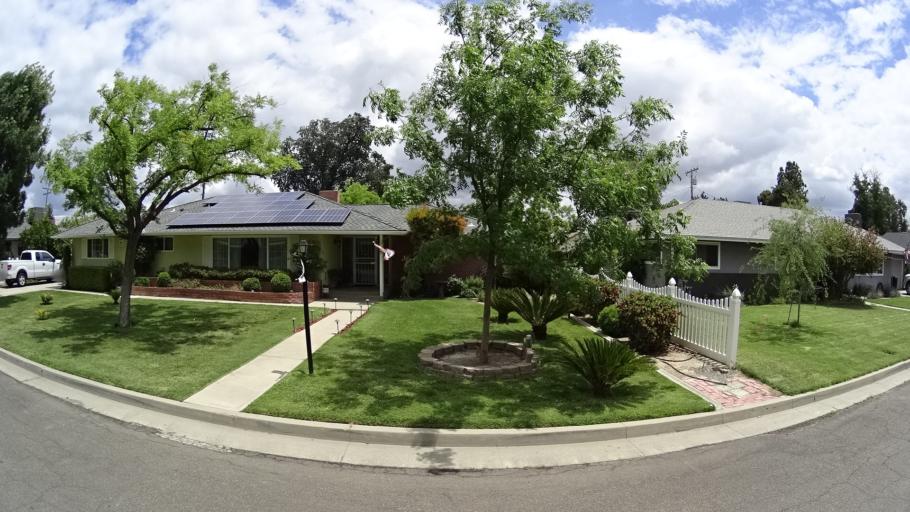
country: US
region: California
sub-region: Kings County
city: Hanford
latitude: 36.3474
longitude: -119.6511
